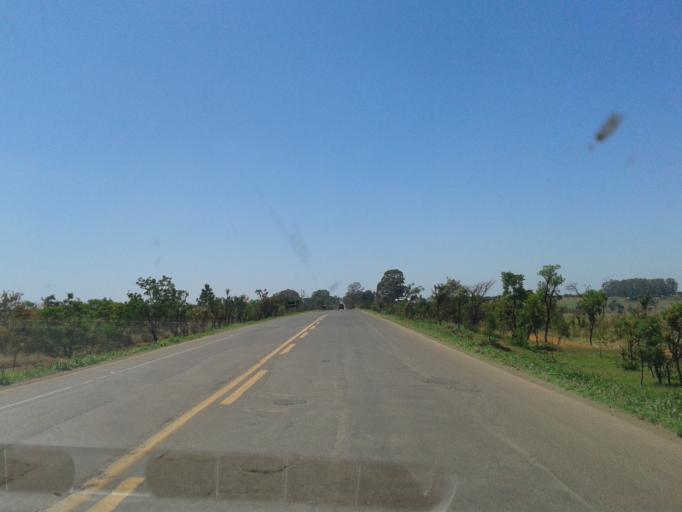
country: BR
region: Minas Gerais
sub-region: Araxa
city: Araxa
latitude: -19.4027
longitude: -47.3181
